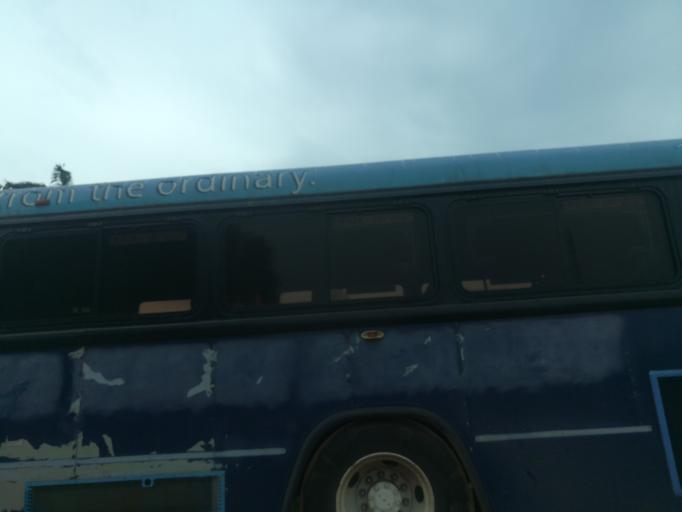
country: NG
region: Oyo
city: Ibadan
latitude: 7.3902
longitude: 3.9316
